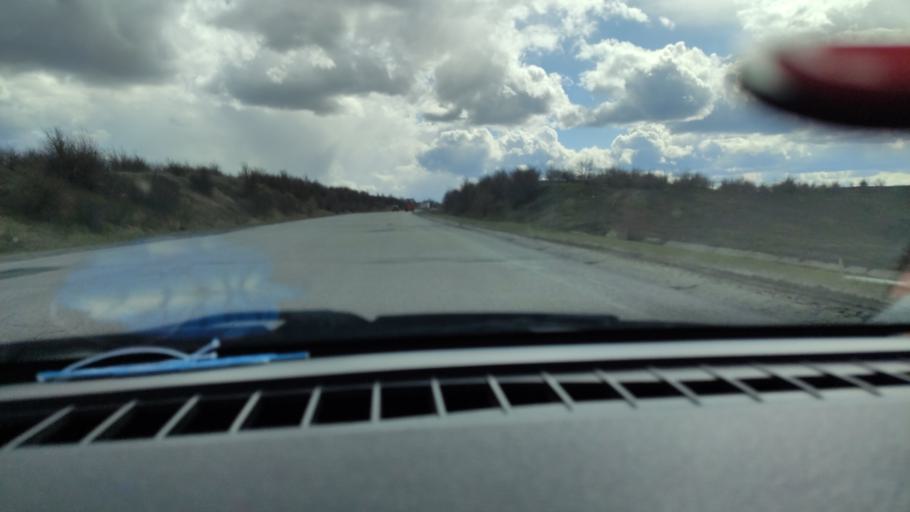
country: RU
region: Samara
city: Varlamovo
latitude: 53.0656
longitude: 48.3533
